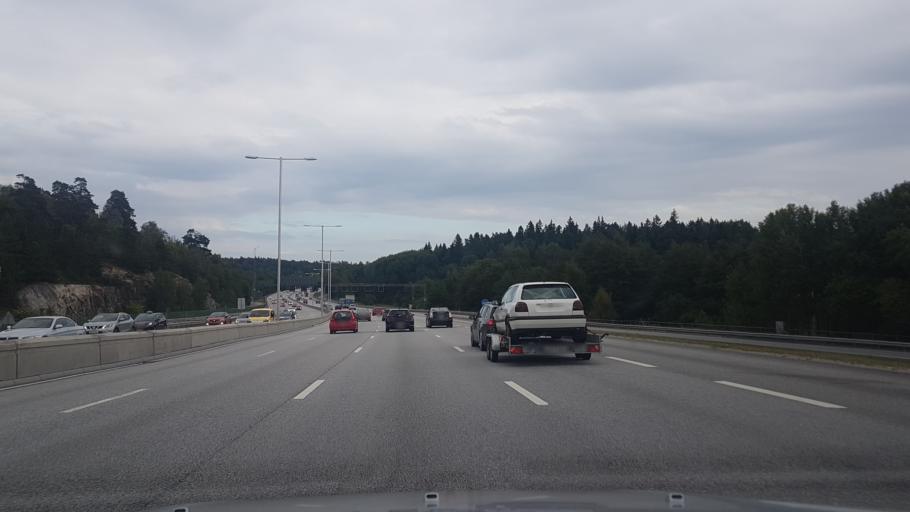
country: SE
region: Stockholm
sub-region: Solna Kommun
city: Rasunda
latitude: 59.3928
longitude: 17.9892
